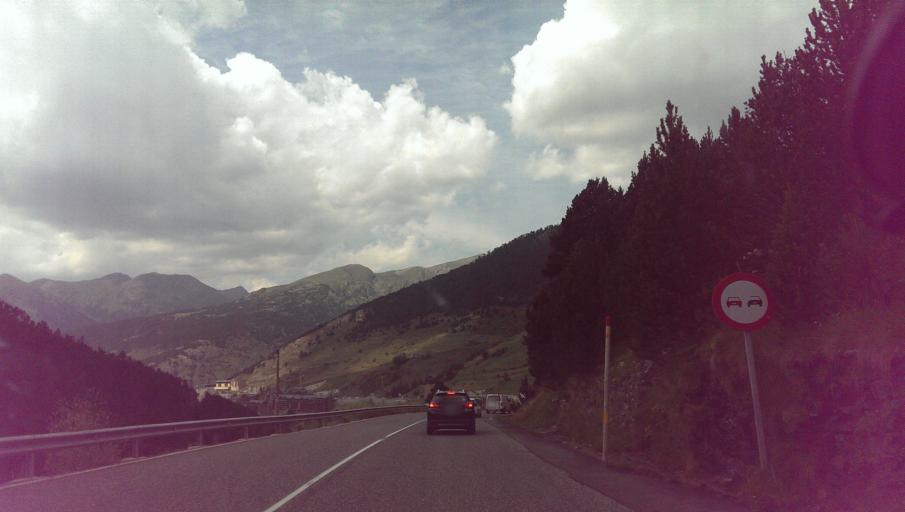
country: AD
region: Canillo
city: El Tarter
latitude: 42.5667
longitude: 1.6789
